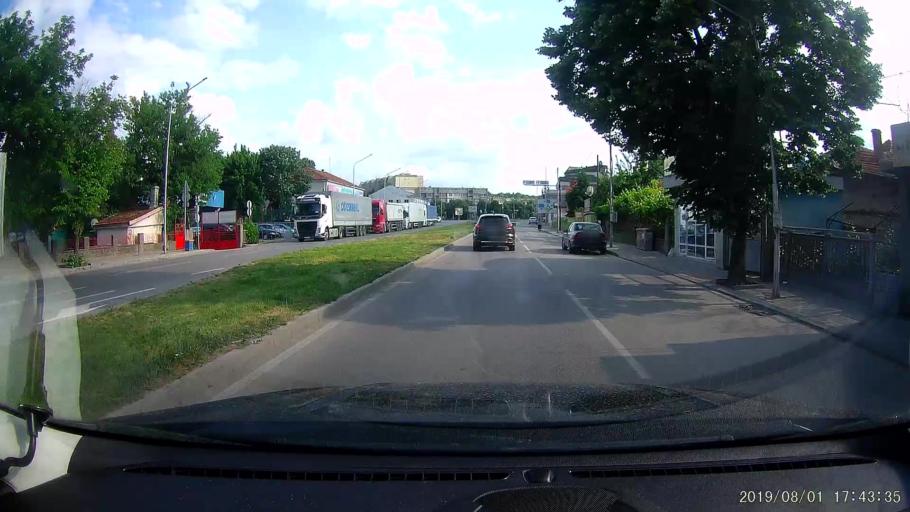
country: BG
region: Silistra
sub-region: Obshtina Silistra
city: Silistra
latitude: 44.1135
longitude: 27.2727
